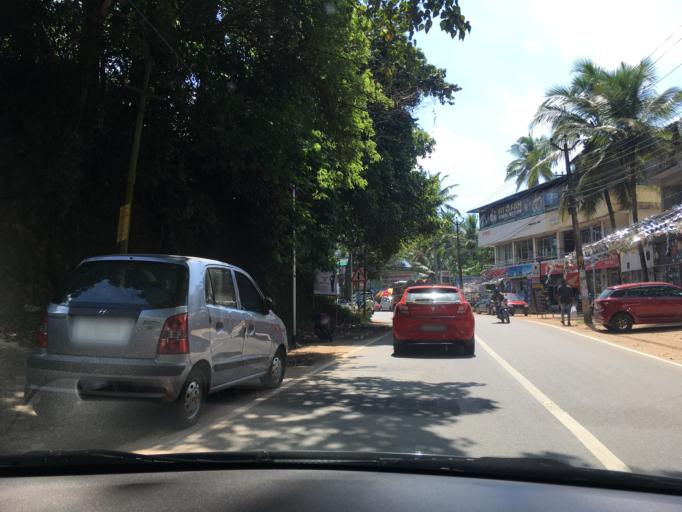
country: IN
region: Kerala
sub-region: Thiruvananthapuram
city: Nedumangad
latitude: 8.6025
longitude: 76.9964
